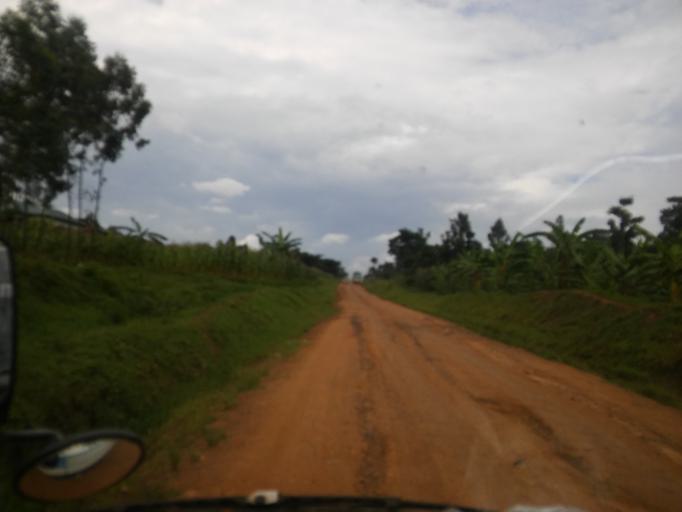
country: UG
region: Eastern Region
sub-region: Bududa District
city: Bududa
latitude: 0.9489
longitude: 34.2491
